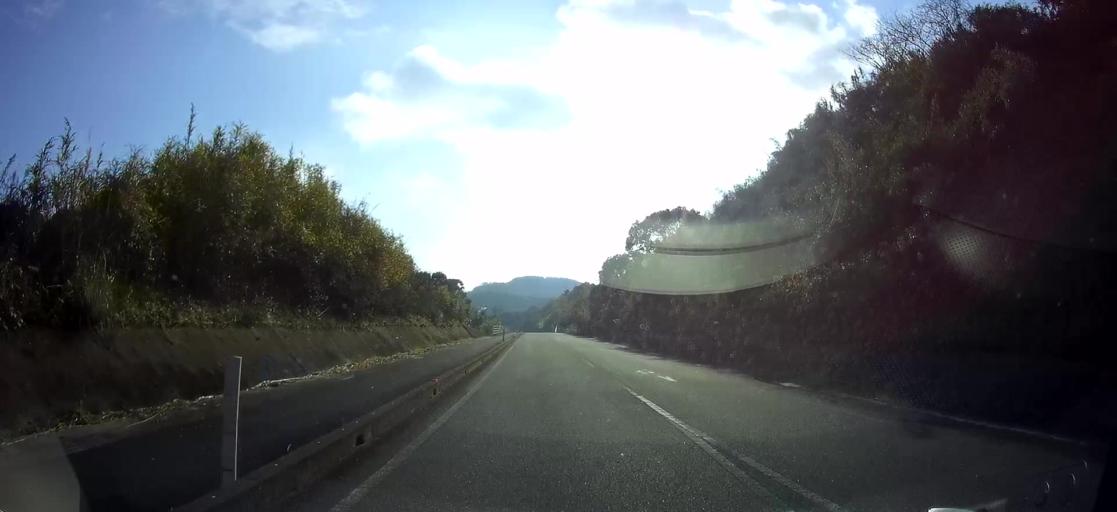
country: JP
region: Kumamoto
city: Yatsushiro
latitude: 32.4706
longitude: 130.4326
